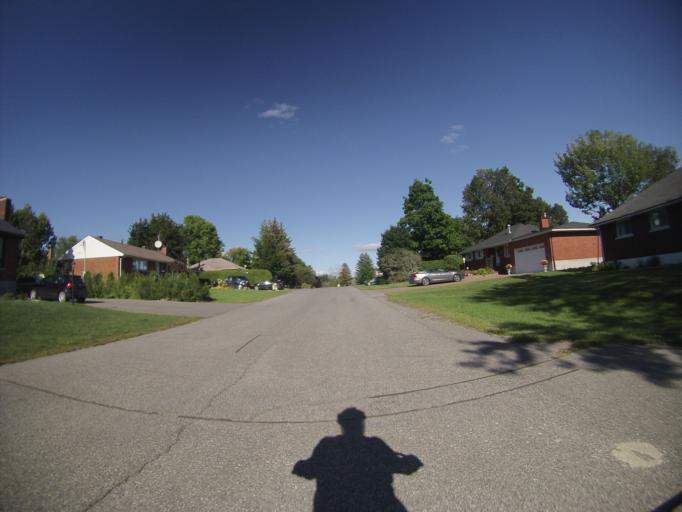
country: CA
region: Ontario
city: Ottawa
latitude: 45.3501
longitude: -75.7402
